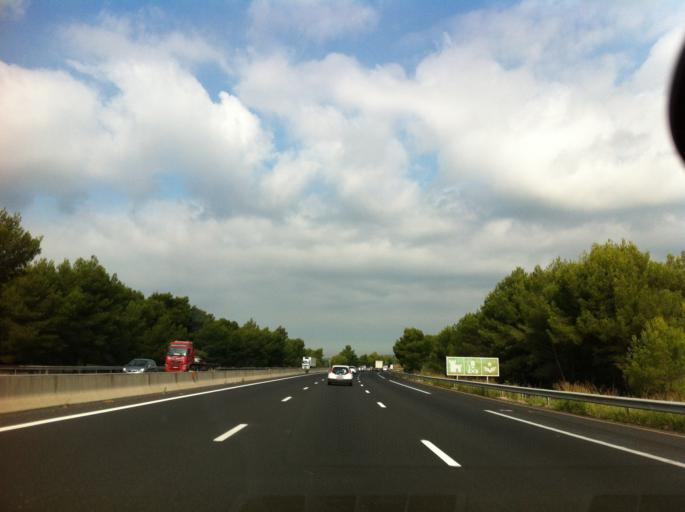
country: FR
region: Provence-Alpes-Cote d'Azur
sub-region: Departement des Bouches-du-Rhone
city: Lancon-Provence
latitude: 43.6014
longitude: 5.1547
